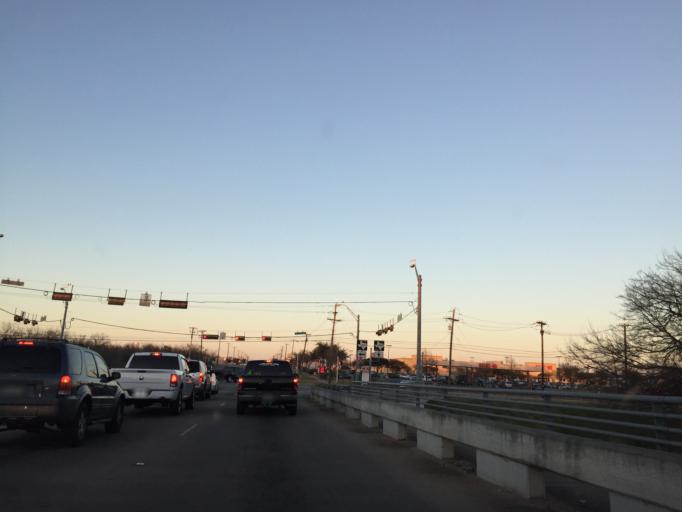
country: US
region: Texas
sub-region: Travis County
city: Pflugerville
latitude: 30.4360
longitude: -97.6142
